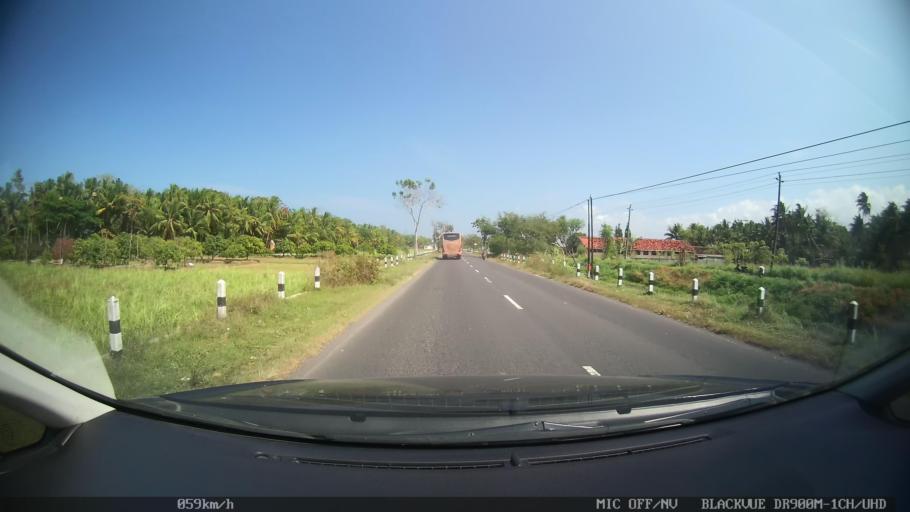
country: ID
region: Daerah Istimewa Yogyakarta
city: Srandakan
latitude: -7.9418
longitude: 110.1656
